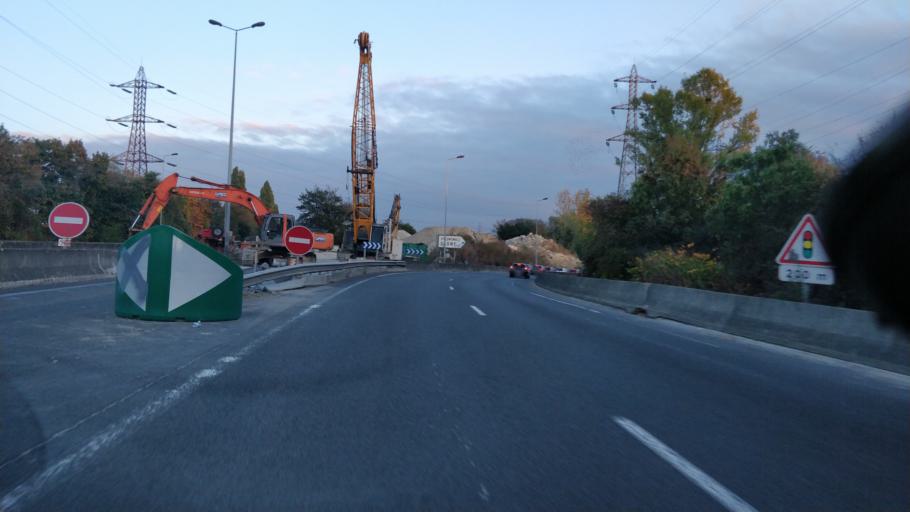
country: FR
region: Ile-de-France
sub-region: Departement de Seine-Saint-Denis
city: Villemomble
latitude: 48.8849
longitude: 2.4901
